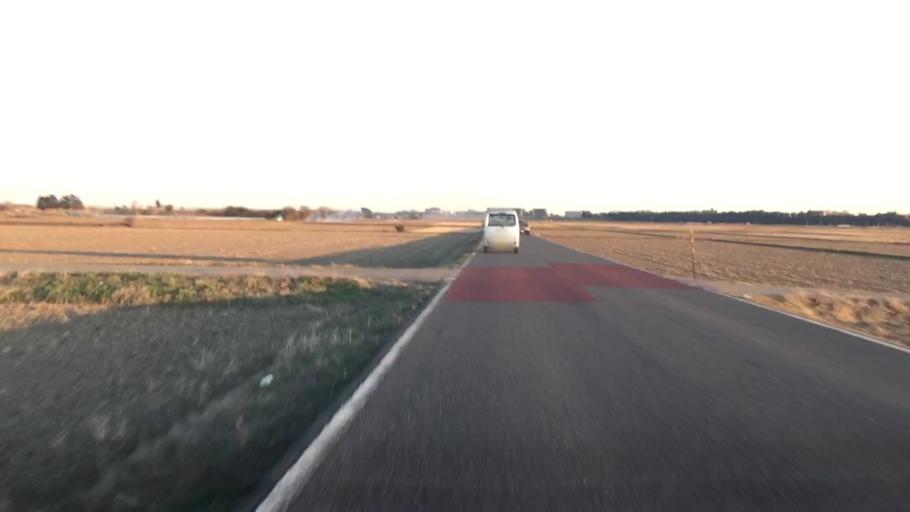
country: JP
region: Chiba
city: Abiko
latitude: 35.8953
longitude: 140.0217
